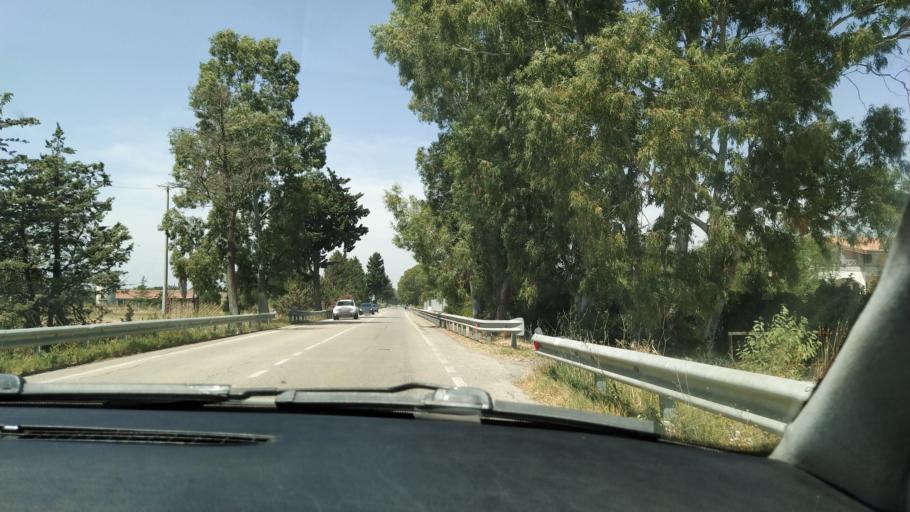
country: IT
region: Apulia
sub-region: Provincia di Taranto
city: Marina di Ginosa
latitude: 40.3739
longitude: 16.8007
